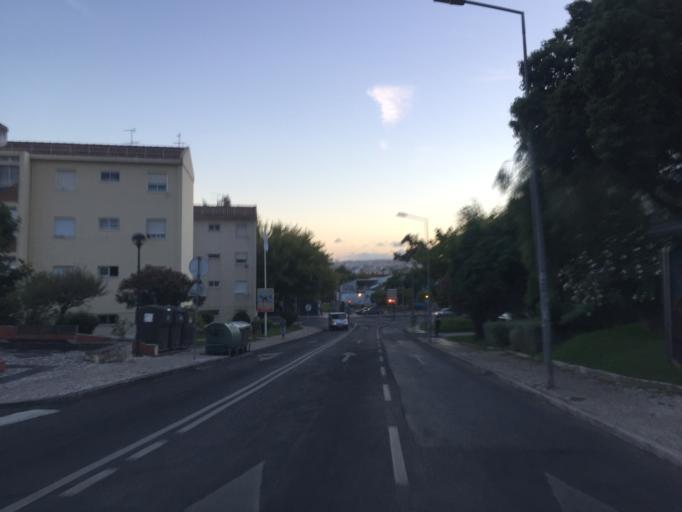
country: PT
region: Lisbon
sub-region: Odivelas
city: Odivelas
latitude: 38.7955
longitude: -9.1797
